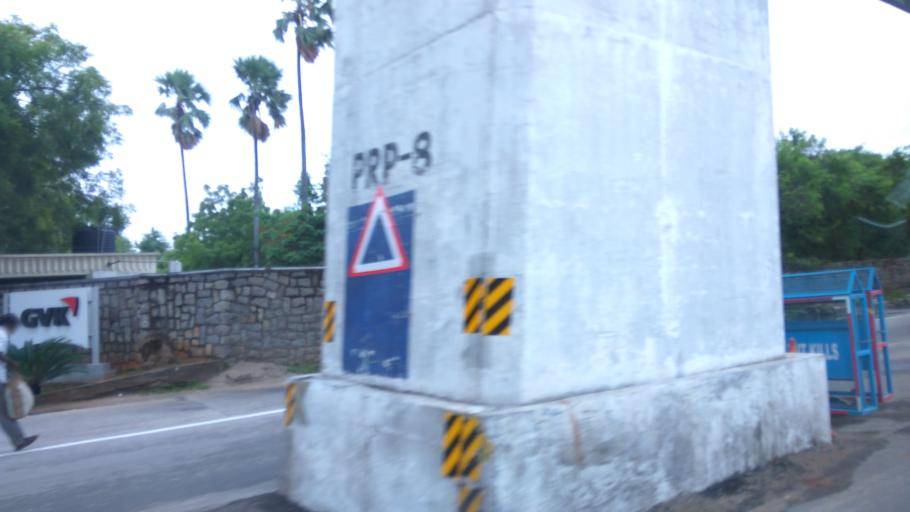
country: IN
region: Telangana
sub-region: Hyderabad
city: Malkajgiri
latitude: 17.4435
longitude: 78.4837
